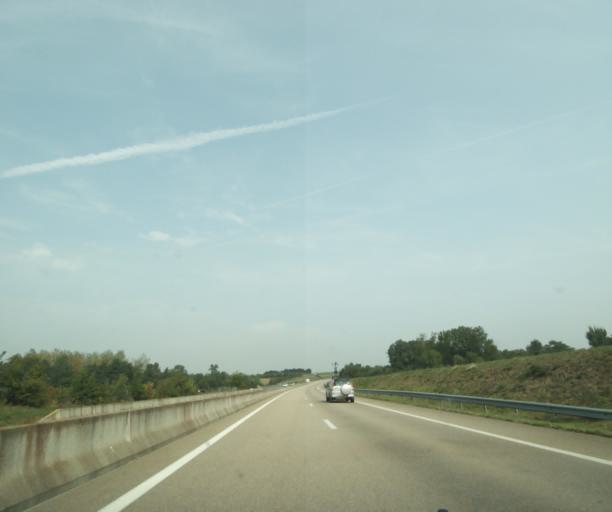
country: FR
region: Lower Normandy
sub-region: Departement de l'Orne
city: Ecouche
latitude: 48.7859
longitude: -0.1253
